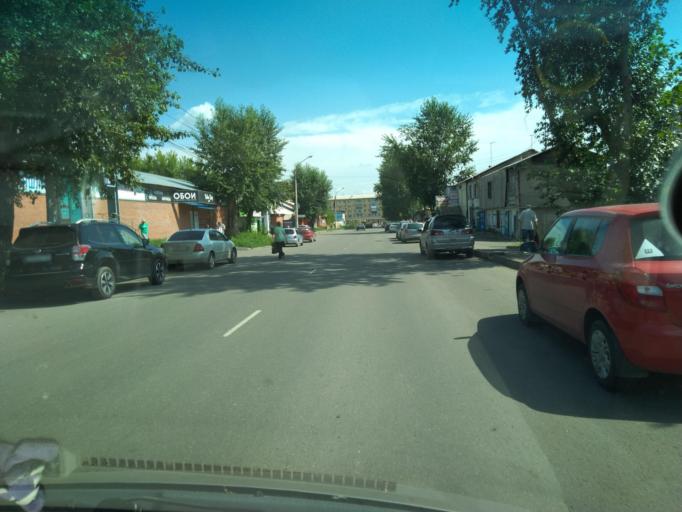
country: RU
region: Krasnoyarskiy
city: Krasnoyarsk
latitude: 56.0286
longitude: 92.8950
